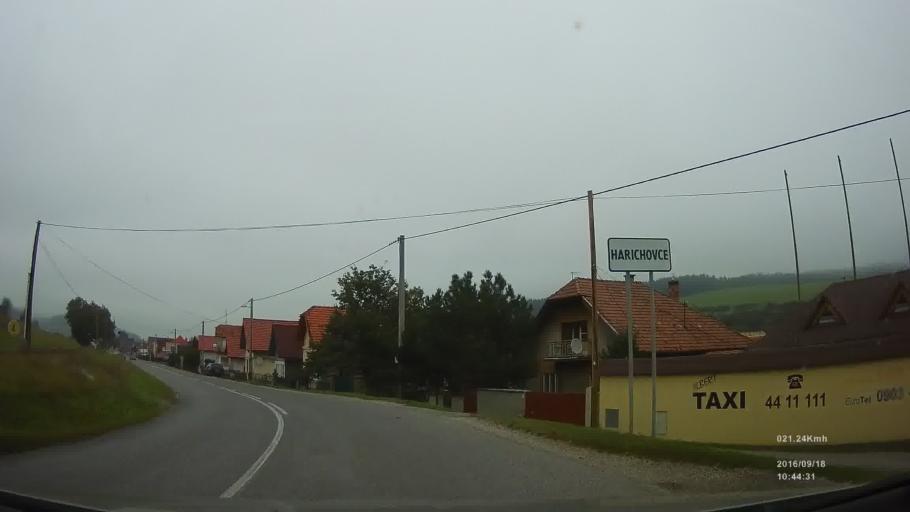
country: SK
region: Kosicky
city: Spisska Nova Ves
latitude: 48.9558
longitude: 20.5840
